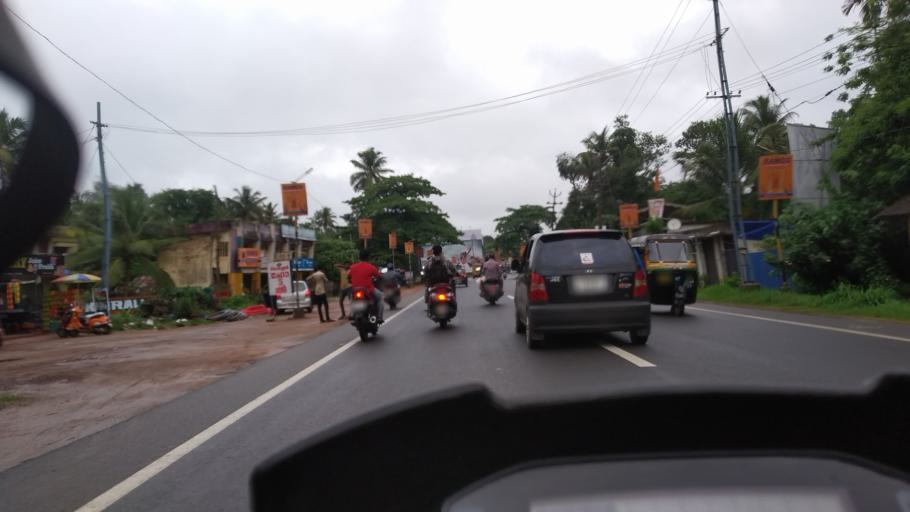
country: IN
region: Kerala
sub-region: Alappuzha
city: Mavelikara
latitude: 9.2813
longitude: 76.4484
